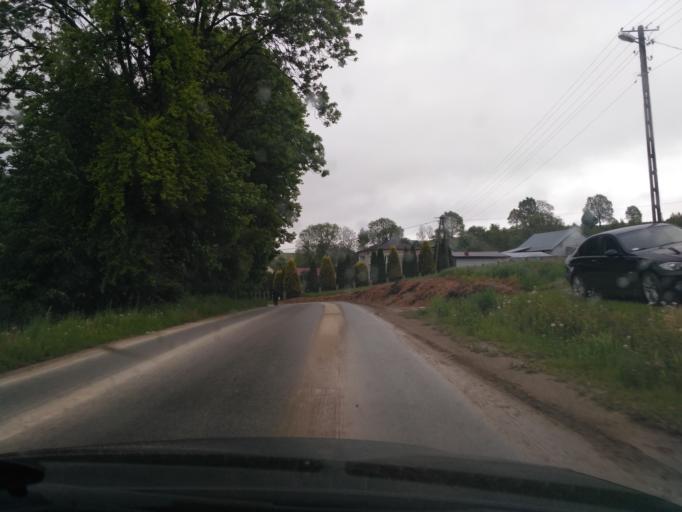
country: PL
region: Subcarpathian Voivodeship
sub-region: Powiat debicki
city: Jodlowa
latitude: 49.8715
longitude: 21.2797
